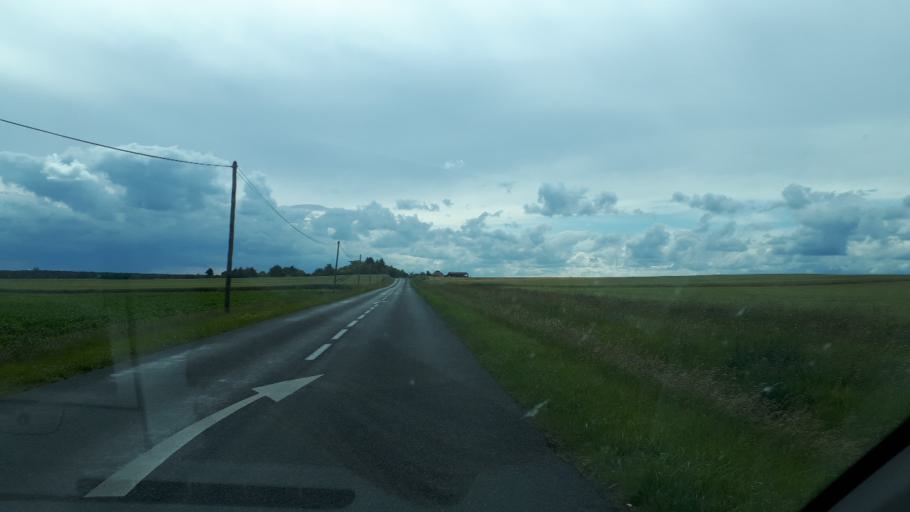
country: FR
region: Centre
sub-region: Departement du Cher
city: Mehun-sur-Yevre
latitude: 47.0815
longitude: 2.2139
